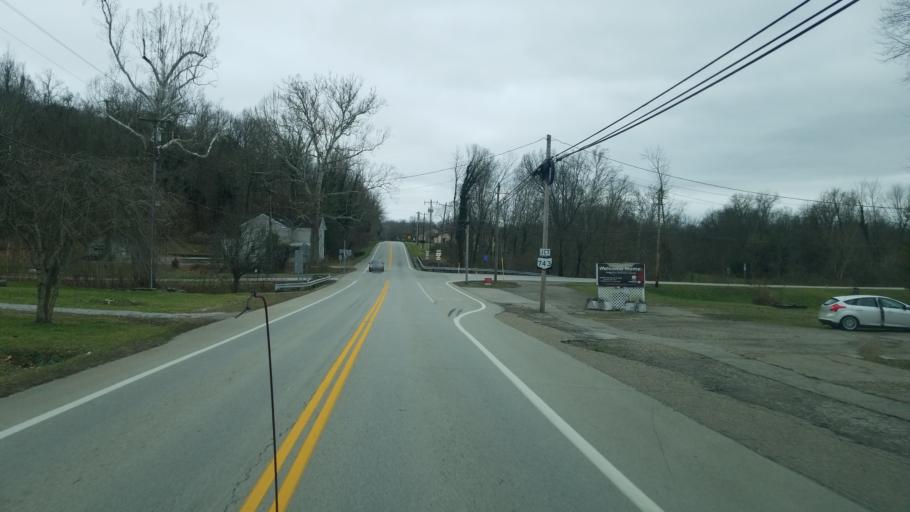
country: US
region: Ohio
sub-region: Clermont County
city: New Richmond
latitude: 38.8589
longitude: -84.2239
